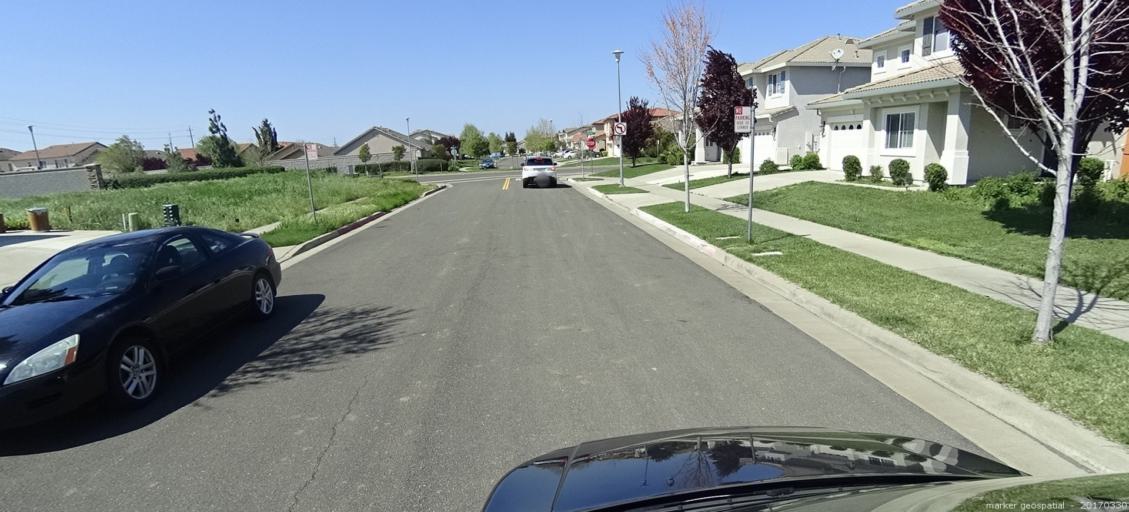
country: US
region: California
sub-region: Sacramento County
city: Laguna
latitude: 38.4393
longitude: -121.4080
